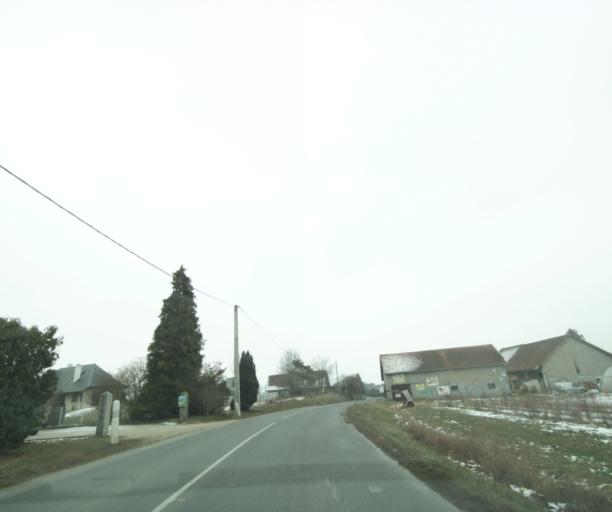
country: FR
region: Rhone-Alpes
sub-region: Departement de la Haute-Savoie
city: Reignier-Esery
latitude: 46.1408
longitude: 6.2806
